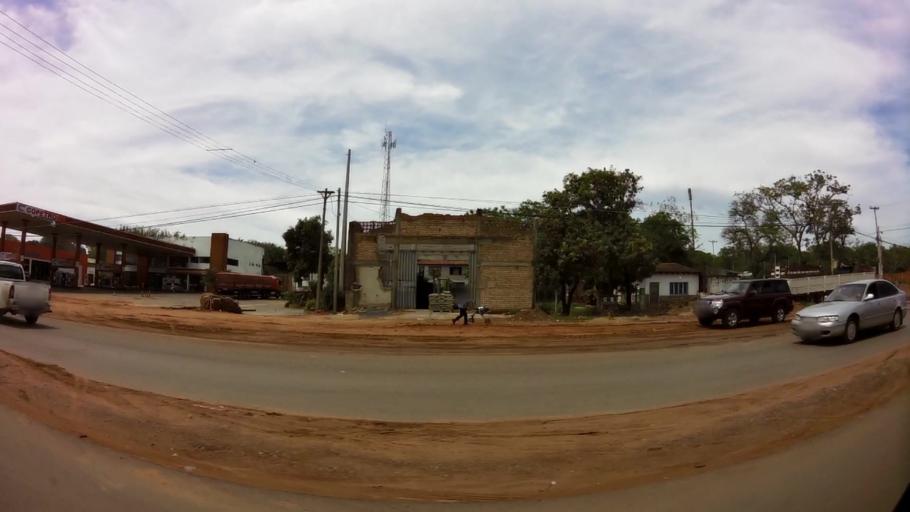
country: PY
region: Central
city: Limpio
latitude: -25.1974
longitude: -57.5156
